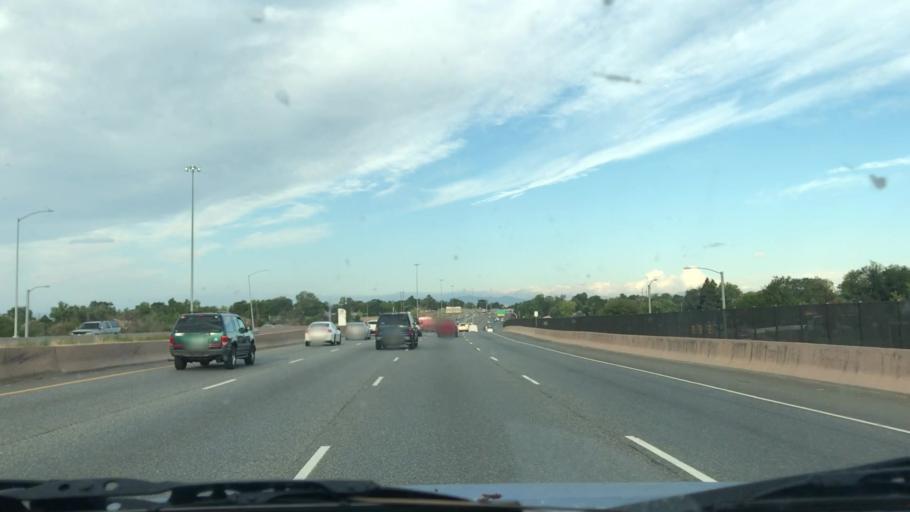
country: US
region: Colorado
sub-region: Adams County
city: Sherrelwood
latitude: 39.8278
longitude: -104.9862
